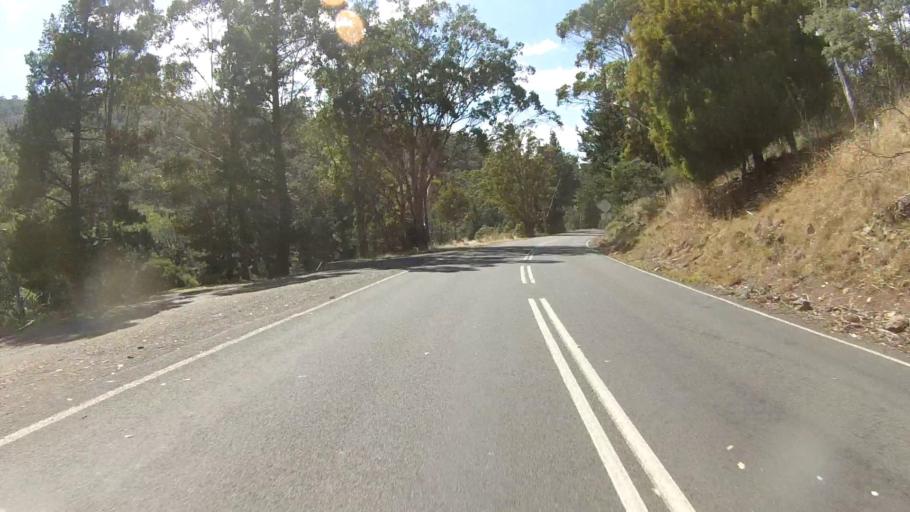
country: AU
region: Tasmania
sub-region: Derwent Valley
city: New Norfolk
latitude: -42.6806
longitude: 146.7467
